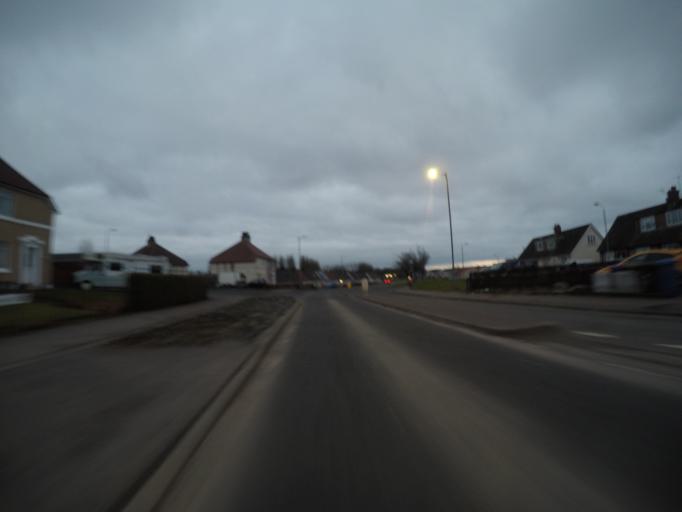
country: GB
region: Scotland
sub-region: North Ayrshire
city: Kilwinning
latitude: 55.6514
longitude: -4.6998
